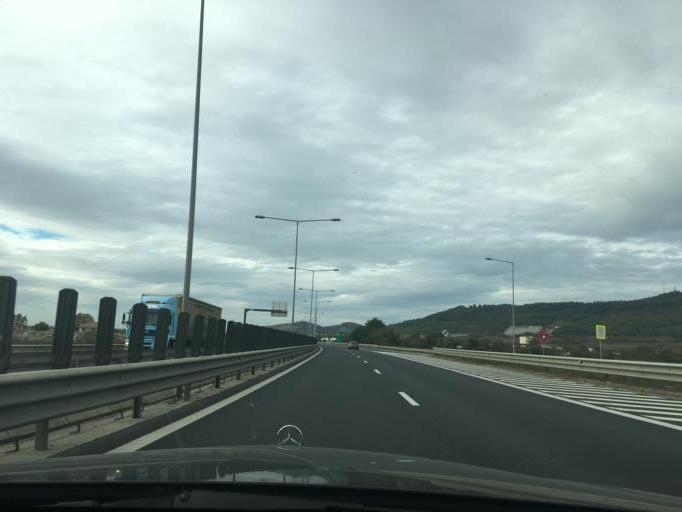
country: RO
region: Sibiu
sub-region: Comuna Selimbar
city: Selimbar
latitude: 45.7901
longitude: 24.1987
